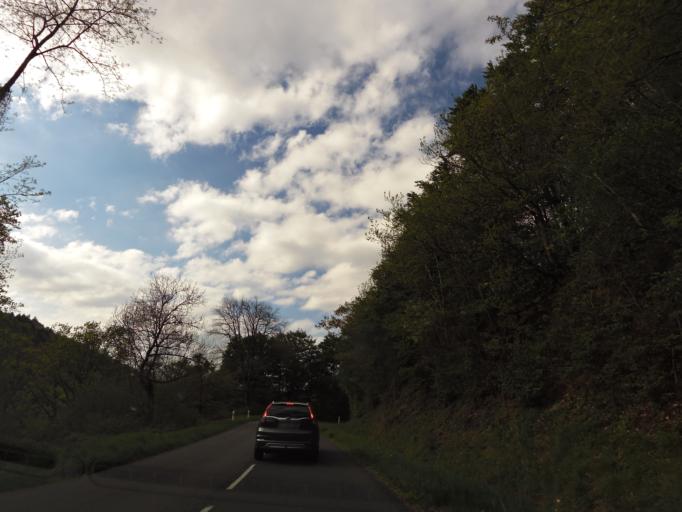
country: FR
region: Midi-Pyrenees
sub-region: Departement du Tarn
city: Soreze
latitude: 43.4257
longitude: 2.0569
